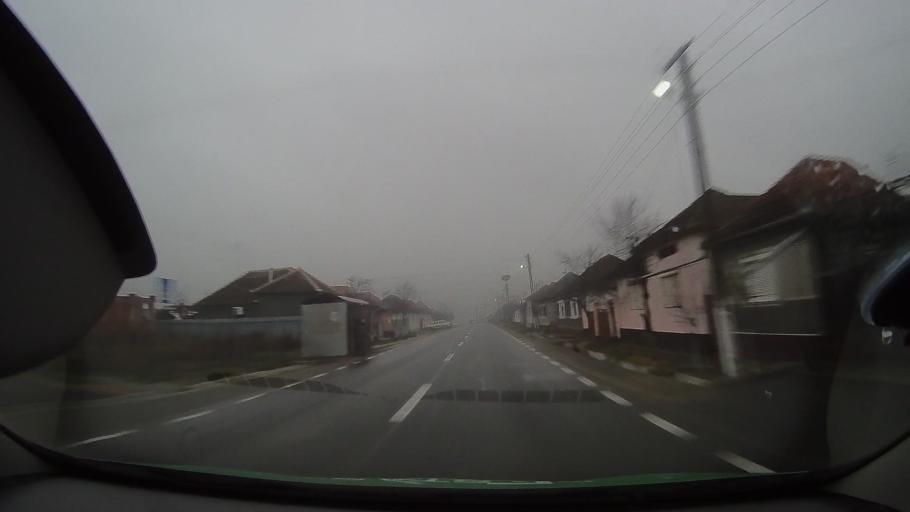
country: RO
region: Arad
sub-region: Comuna Craiova
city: Craiova
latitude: 46.6297
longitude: 21.9589
